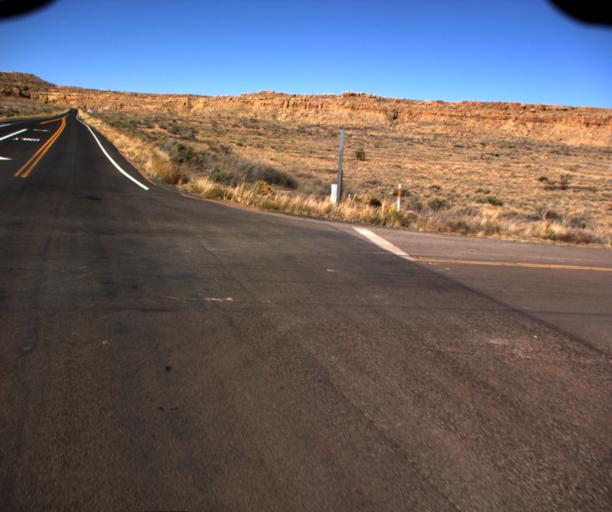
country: US
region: Arizona
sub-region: Navajo County
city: First Mesa
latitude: 35.8793
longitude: -110.6126
